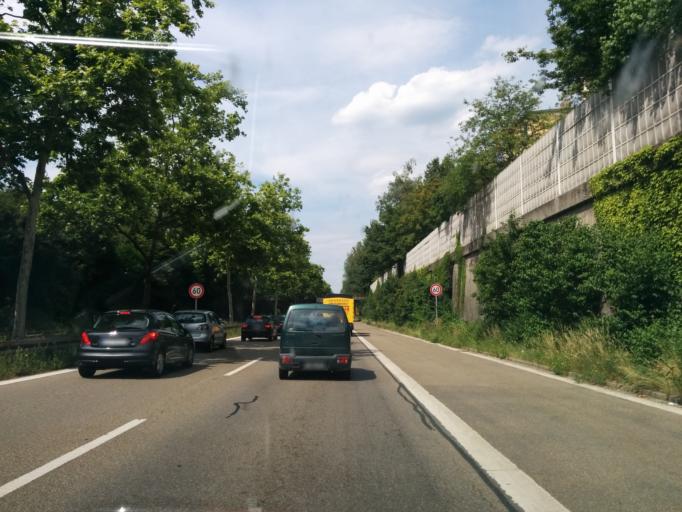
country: DE
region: Bavaria
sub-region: Regierungsbezirk Mittelfranken
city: Nuernberg
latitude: 49.4351
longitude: 11.0631
